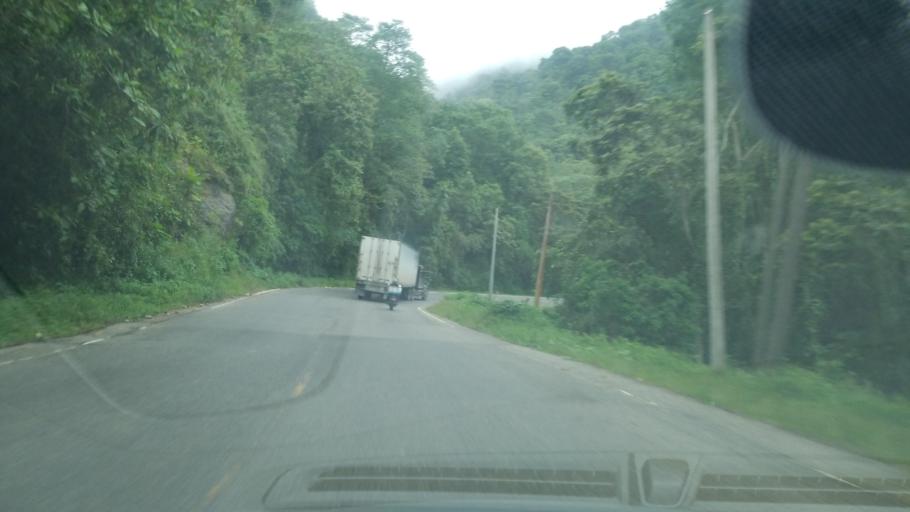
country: HN
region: Ocotepeque
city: La Labor
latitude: 14.4744
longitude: -89.0588
